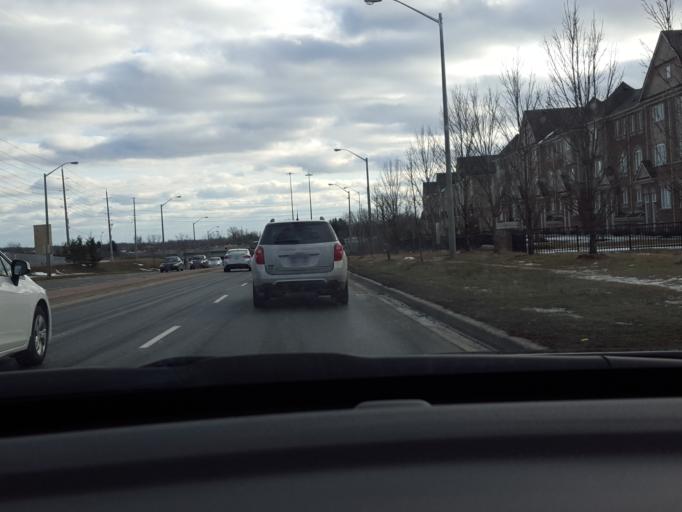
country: CA
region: Ontario
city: Ajax
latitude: 43.8594
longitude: -79.0143
